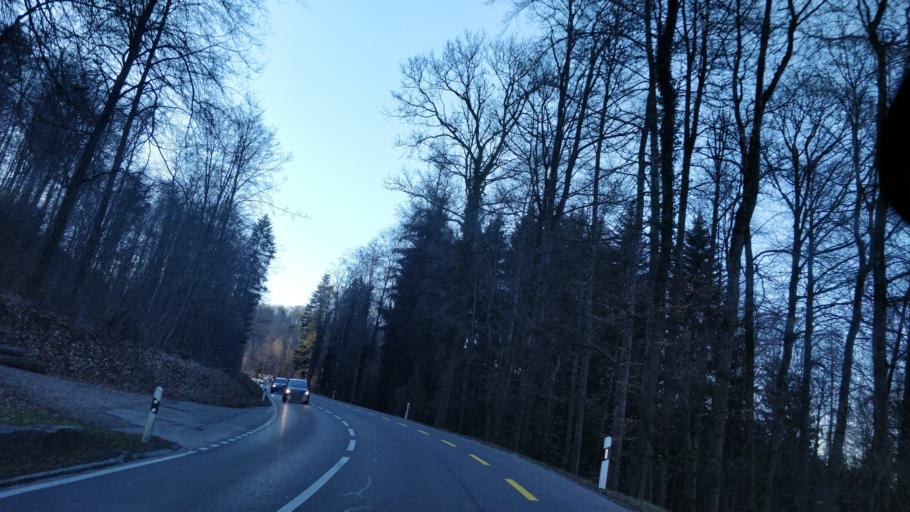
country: CH
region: Zurich
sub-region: Bezirk Buelach
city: Rorbas
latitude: 47.5214
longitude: 8.5743
